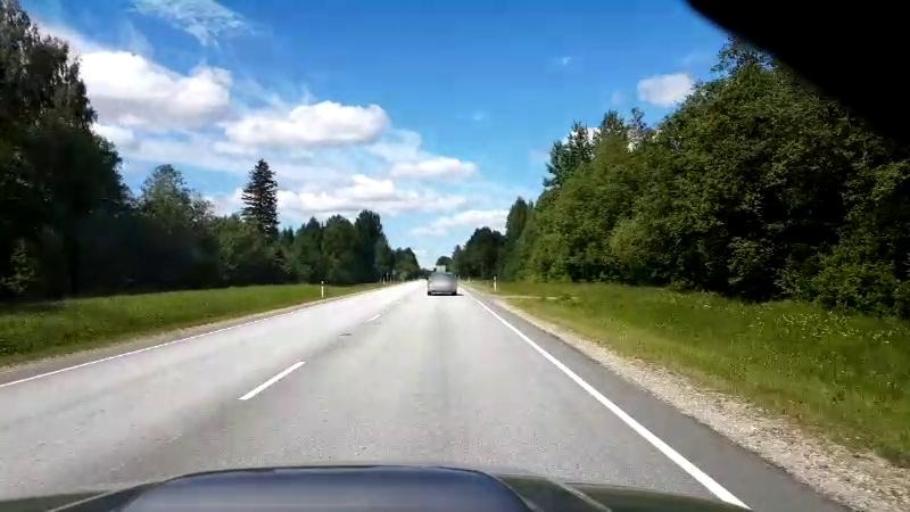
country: EE
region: Paernumaa
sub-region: Halinga vald
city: Parnu-Jaagupi
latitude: 58.5528
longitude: 24.5314
